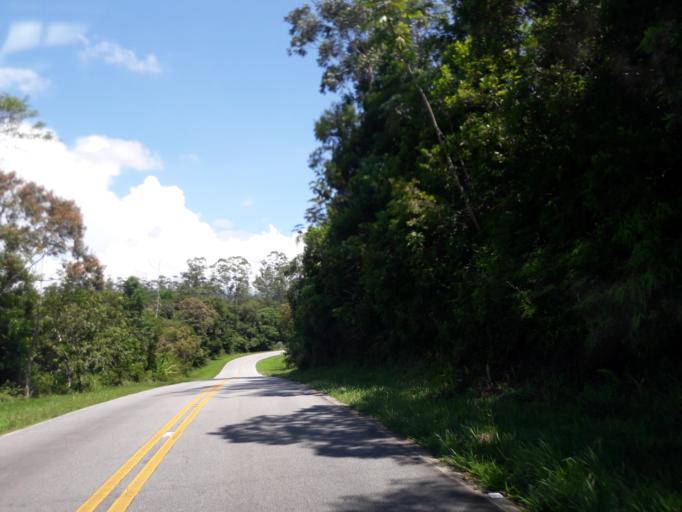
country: BR
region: Parana
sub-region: Antonina
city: Antonina
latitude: -25.5256
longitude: -48.7869
